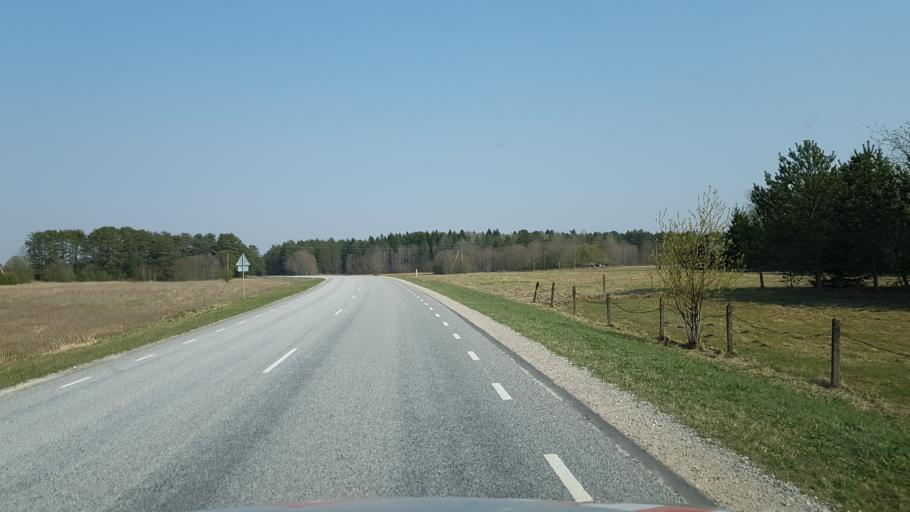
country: EE
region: Harju
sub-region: Paldiski linn
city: Paldiski
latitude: 59.2173
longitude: 24.0484
